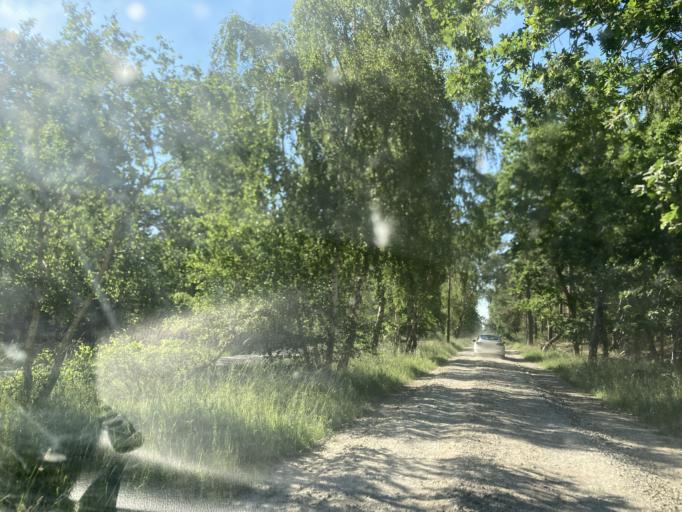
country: DK
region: Capital Region
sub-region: Halsnaes Kommune
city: Frederiksvaerk
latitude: 56.0140
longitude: 12.0172
